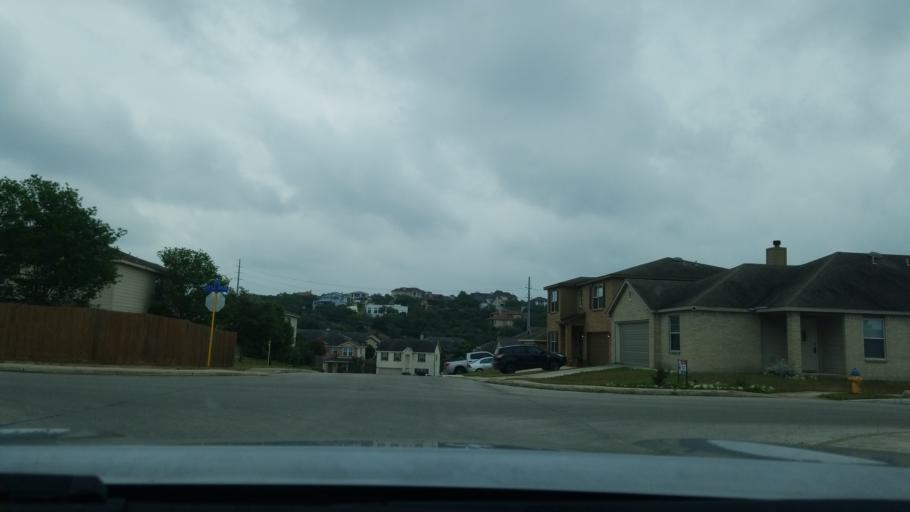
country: US
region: Texas
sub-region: Bexar County
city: Timberwood Park
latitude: 29.6817
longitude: -98.4638
